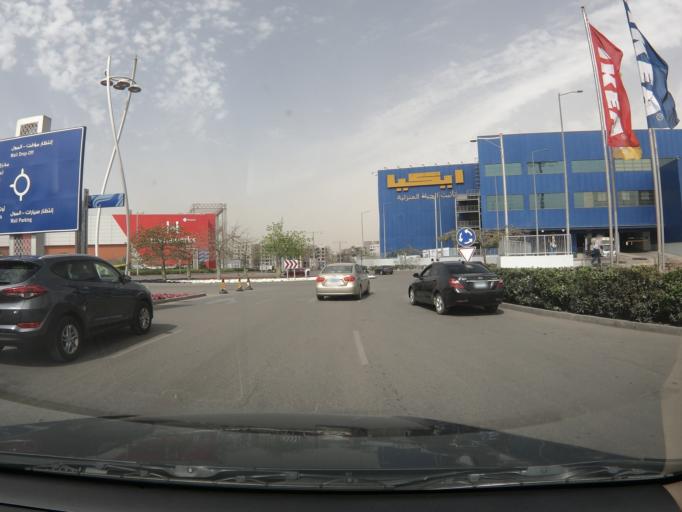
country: EG
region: Muhafazat al Qahirah
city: Cairo
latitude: 30.0298
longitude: 31.4061
